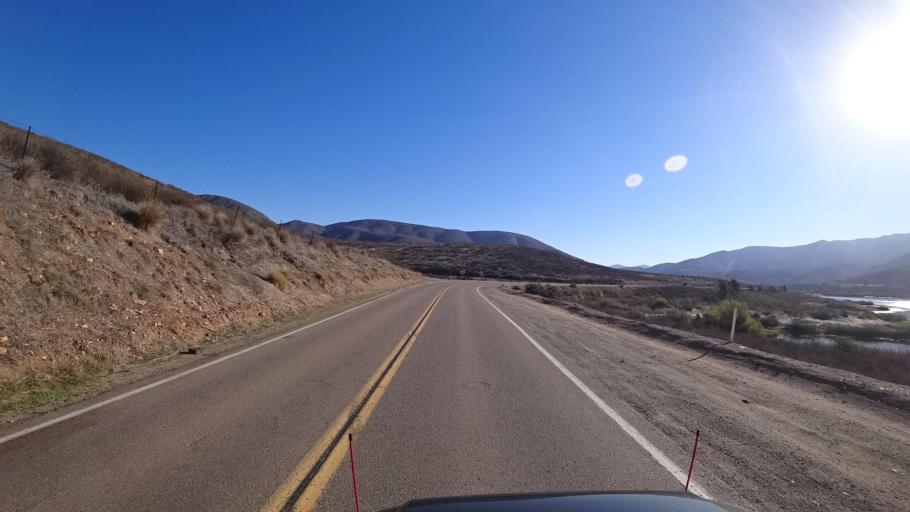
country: US
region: California
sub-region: San Diego County
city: Jamul
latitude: 32.6347
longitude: -116.9130
